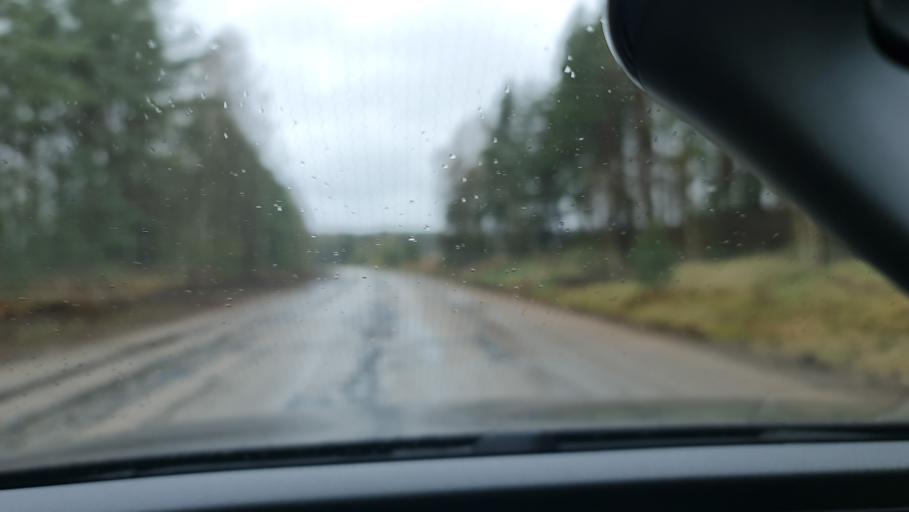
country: RU
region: Novgorod
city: Valday
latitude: 58.0406
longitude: 32.9227
